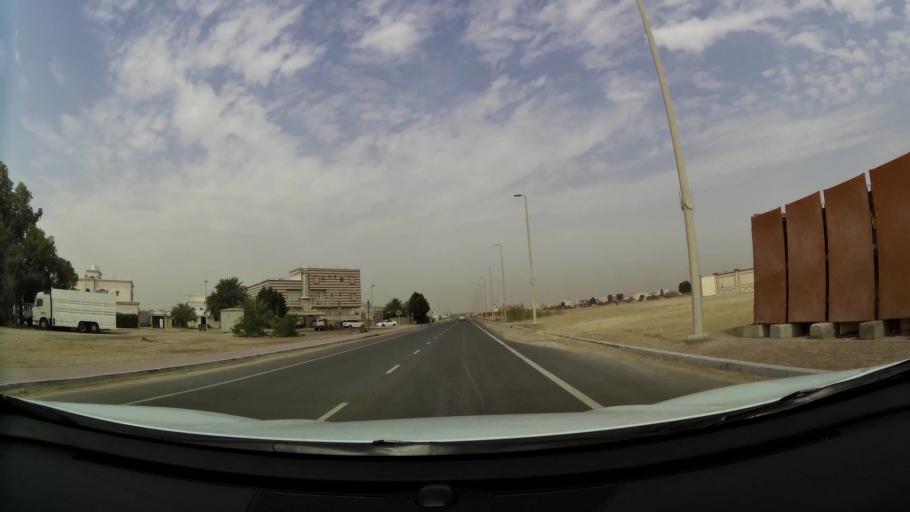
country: AE
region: Abu Dhabi
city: Abu Dhabi
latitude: 24.3242
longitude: 54.6396
